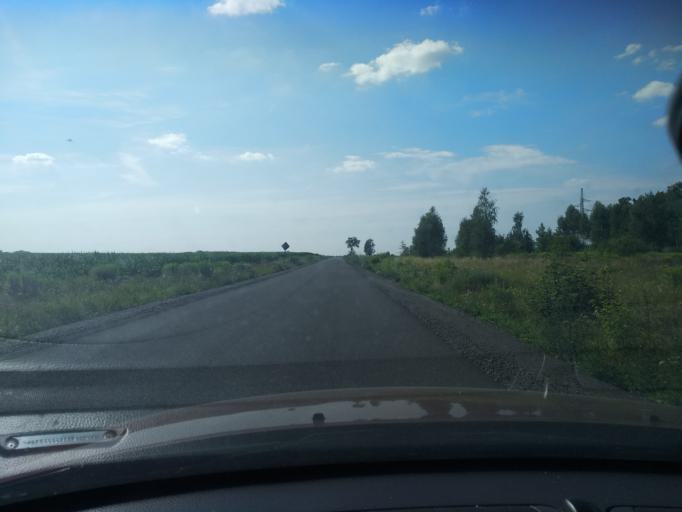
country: PL
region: Lower Silesian Voivodeship
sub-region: Powiat lubanski
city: Lesna
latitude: 51.0446
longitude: 15.2027
